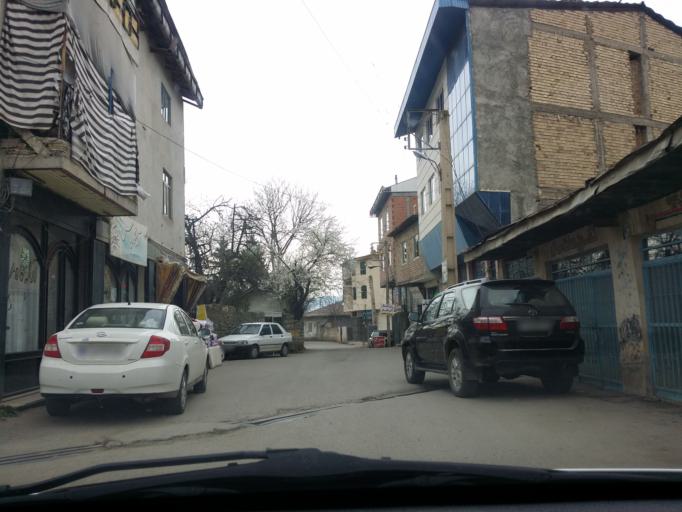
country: IR
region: Mazandaran
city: `Abbasabad
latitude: 36.5075
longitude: 51.1625
